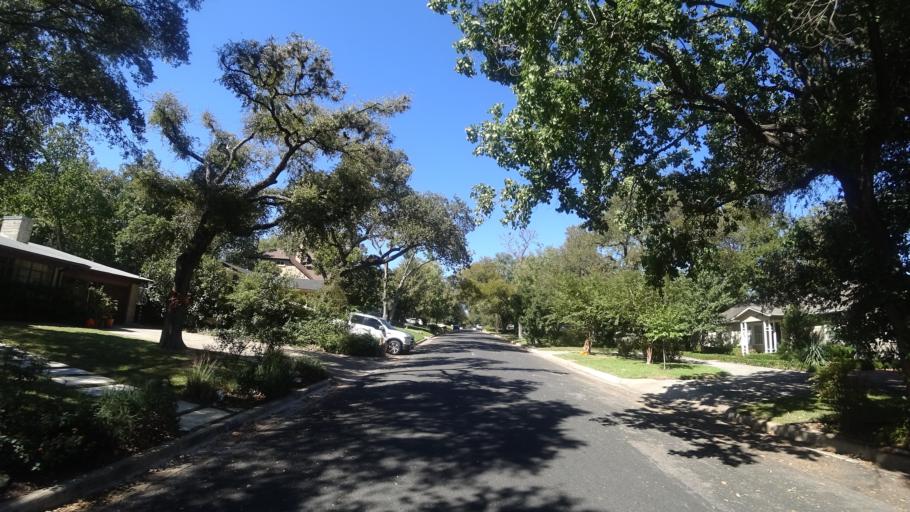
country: US
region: Texas
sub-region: Travis County
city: Austin
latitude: 30.2971
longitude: -97.7616
